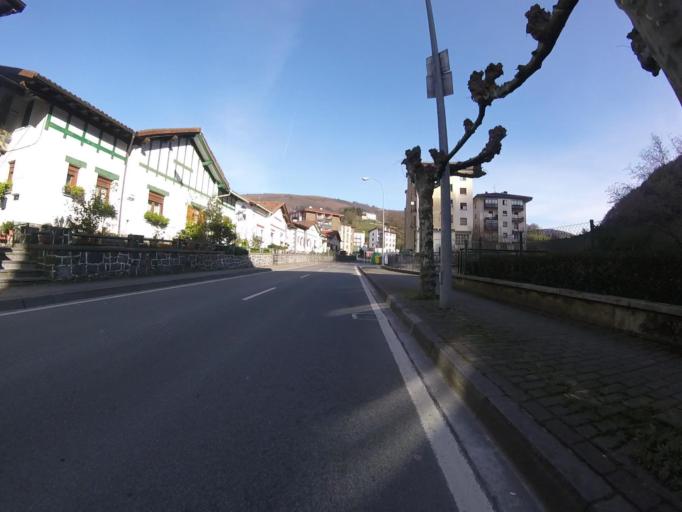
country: ES
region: Navarre
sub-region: Provincia de Navarra
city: Leitza
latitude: 43.0825
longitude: -1.9129
